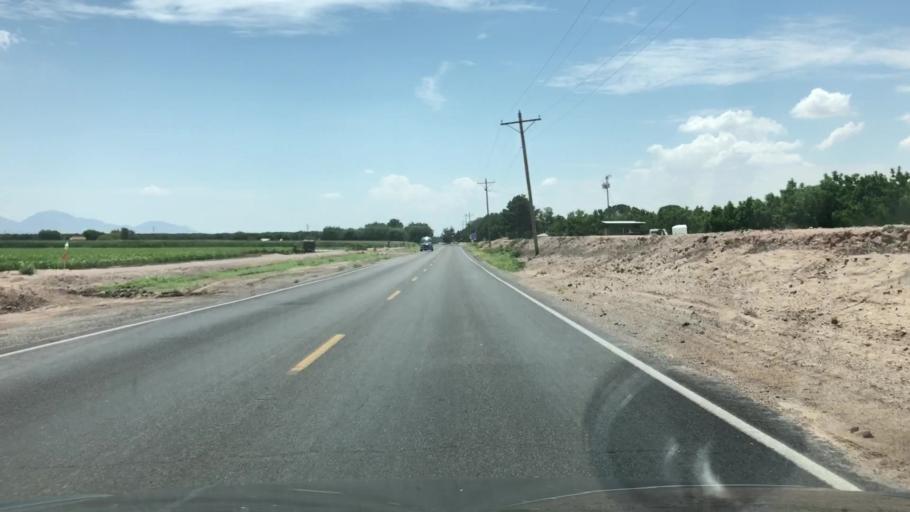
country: US
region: New Mexico
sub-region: Dona Ana County
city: Anthony
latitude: 32.0212
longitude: -106.6700
